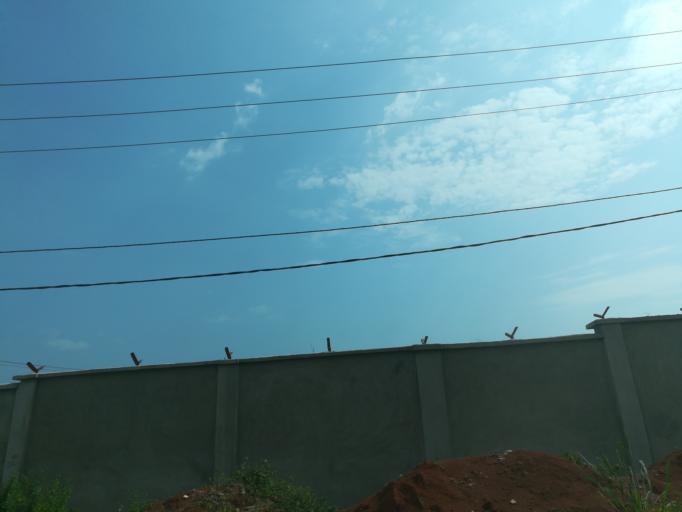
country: NG
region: Lagos
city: Ikorodu
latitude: 6.6401
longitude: 3.6693
